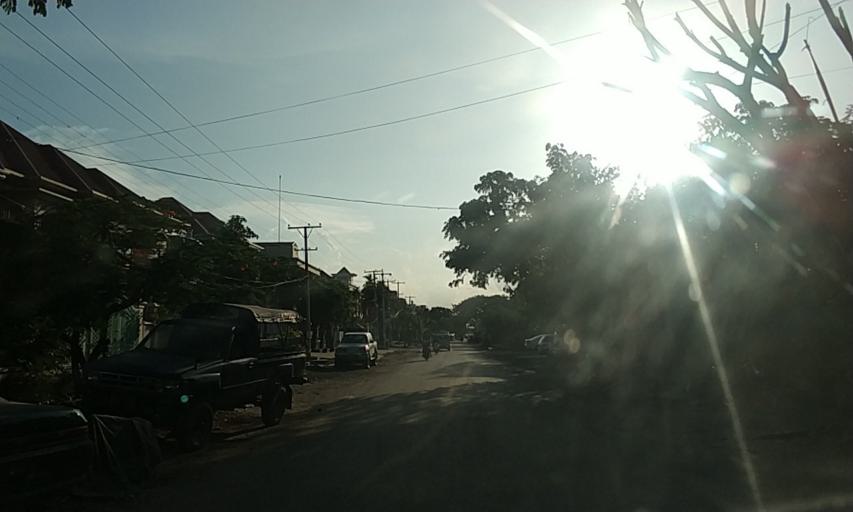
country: MM
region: Mandalay
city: Mandalay
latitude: 21.9700
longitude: 96.1000
